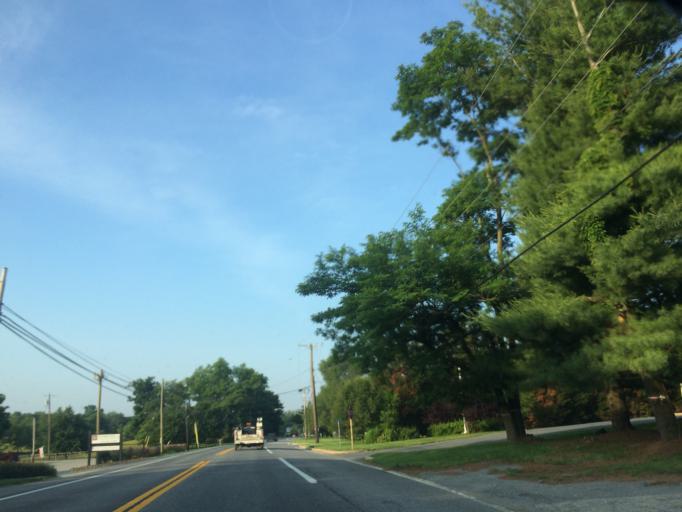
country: US
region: Maryland
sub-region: Carroll County
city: Sykesville
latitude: 39.2889
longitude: -77.0276
